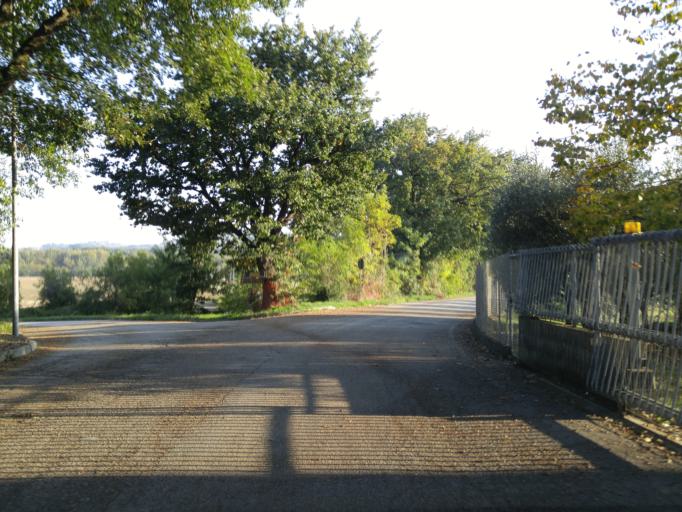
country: IT
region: The Marches
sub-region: Provincia di Pesaro e Urbino
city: Tavernelle
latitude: 43.7149
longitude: 12.8636
